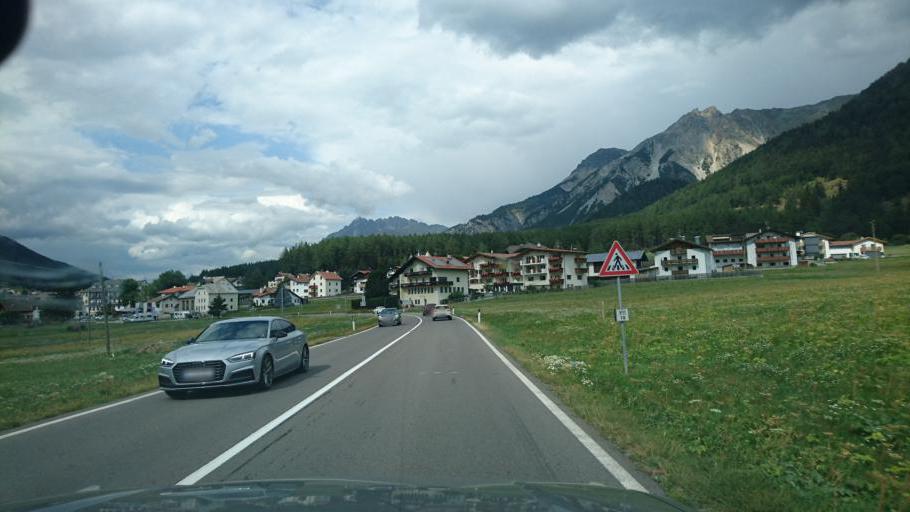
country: IT
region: Trentino-Alto Adige
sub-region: Bolzano
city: Curon Venosta
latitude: 46.7576
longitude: 10.5375
